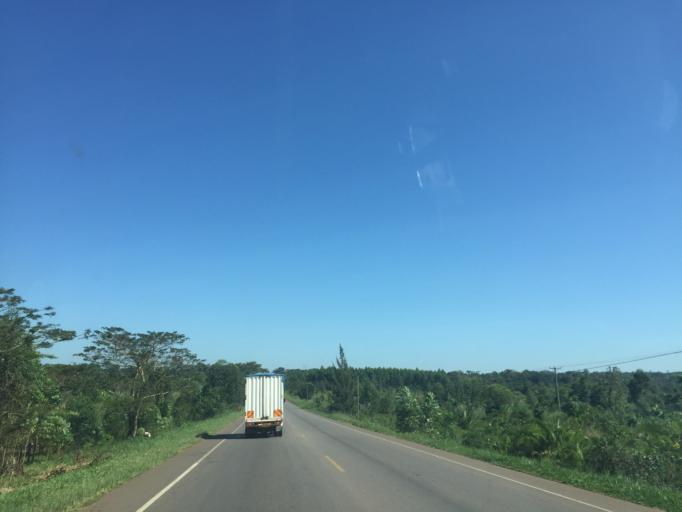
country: UG
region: Central Region
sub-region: Luwero District
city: Wobulenzi
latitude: 0.7881
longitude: 32.5092
